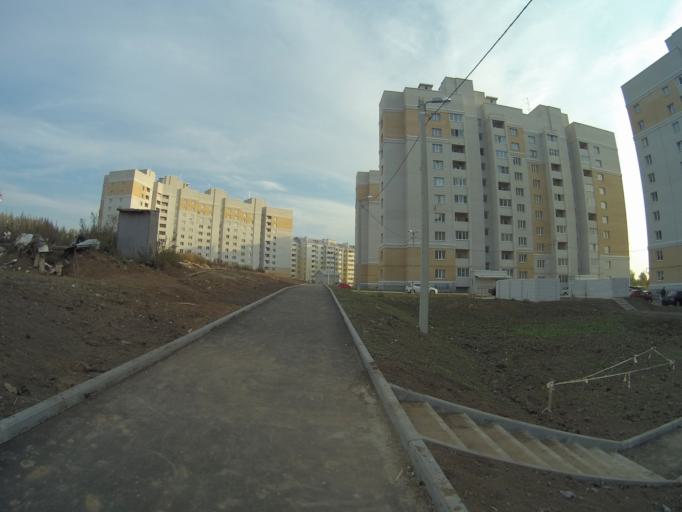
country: RU
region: Vladimir
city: Vladimir
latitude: 56.1615
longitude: 40.3735
